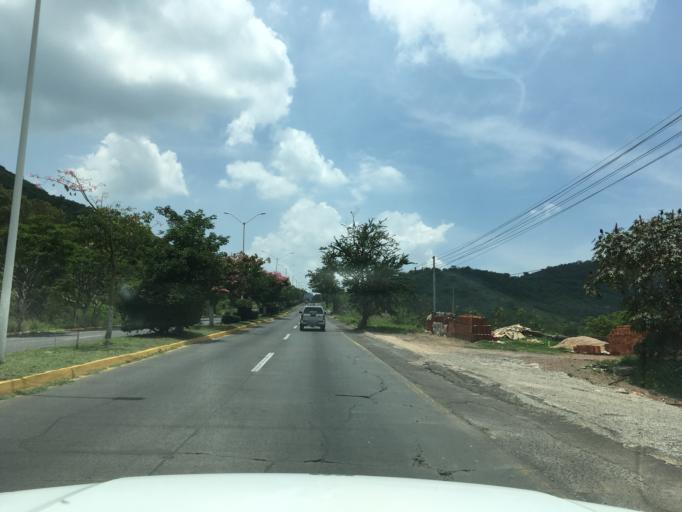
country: MX
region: Jalisco
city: Tlajomulco de Zuniga
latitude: 20.4904
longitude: -103.4718
